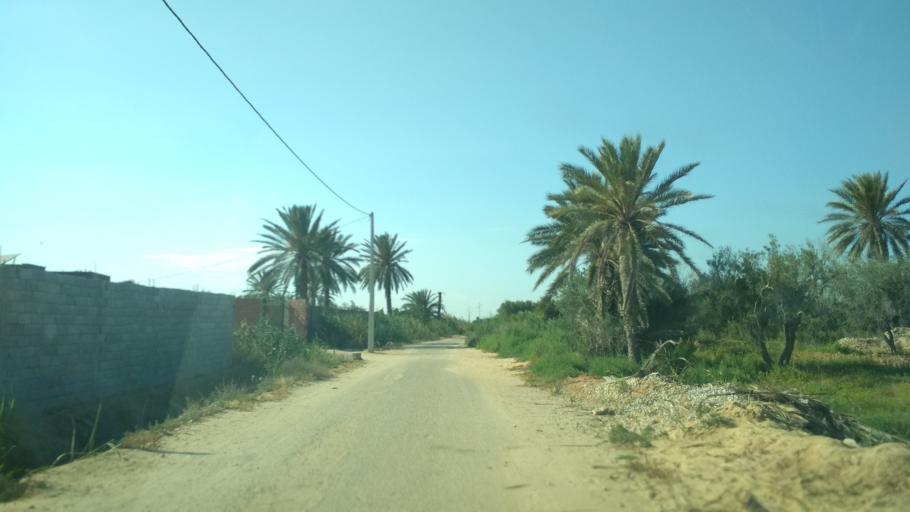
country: TN
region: Qabis
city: Gabes
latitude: 33.9569
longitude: 10.0589
